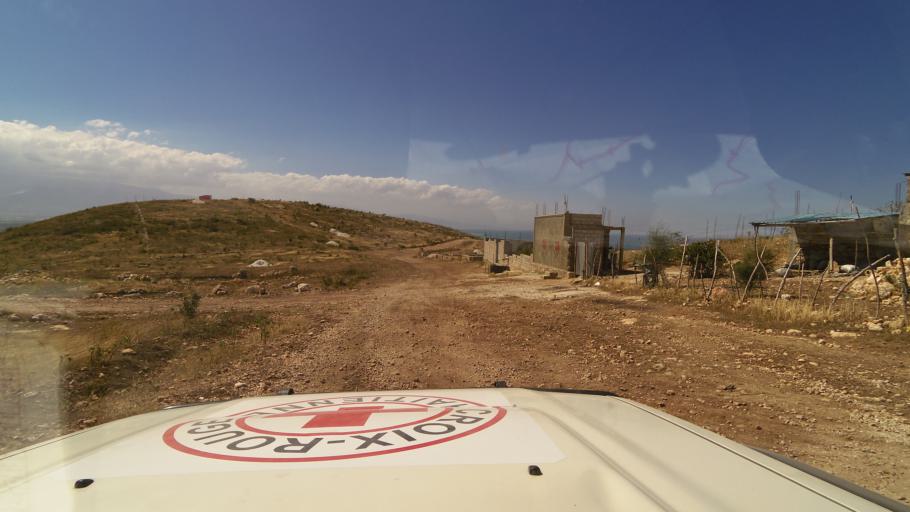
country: HT
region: Ouest
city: Croix des Bouquets
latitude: 18.6759
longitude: -72.2938
